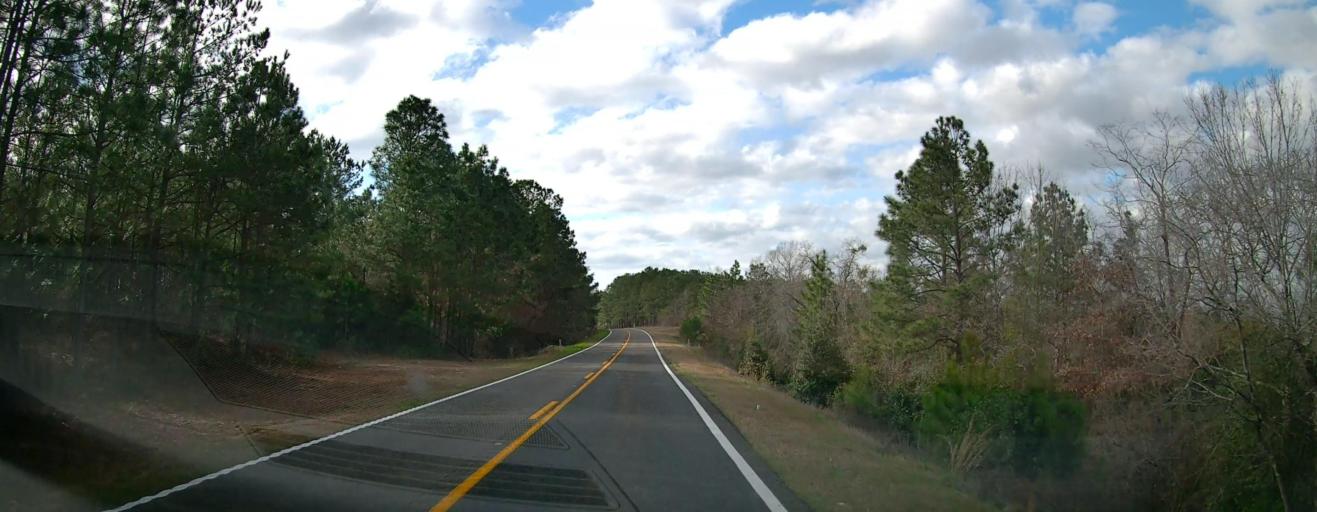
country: US
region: Georgia
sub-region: Marion County
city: Buena Vista
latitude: 32.4422
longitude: -84.5139
